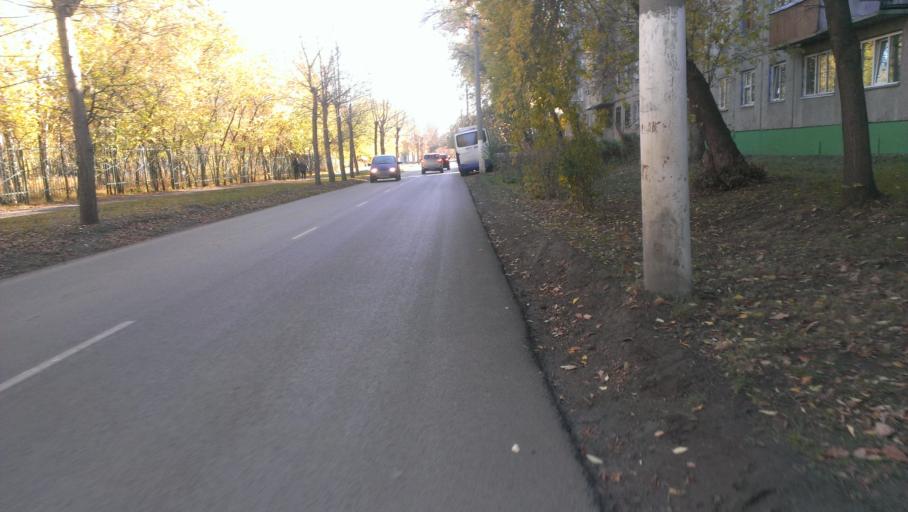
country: RU
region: Altai Krai
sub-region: Gorod Barnaulskiy
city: Barnaul
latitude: 53.3637
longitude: 83.6877
